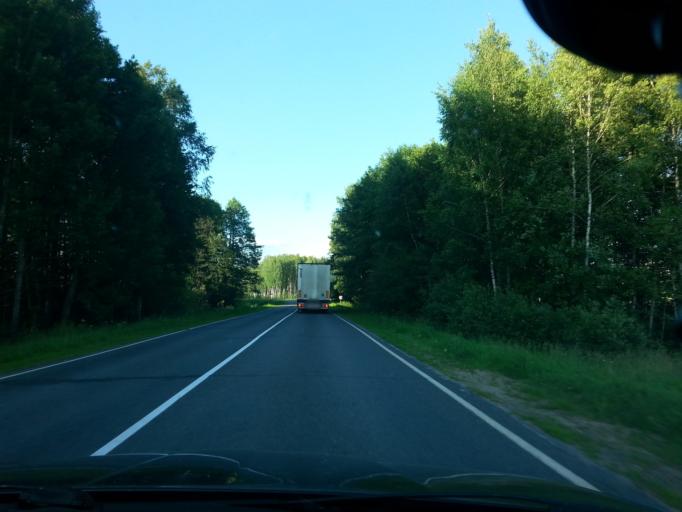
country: BY
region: Minsk
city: Svir
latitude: 54.8798
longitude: 26.3674
